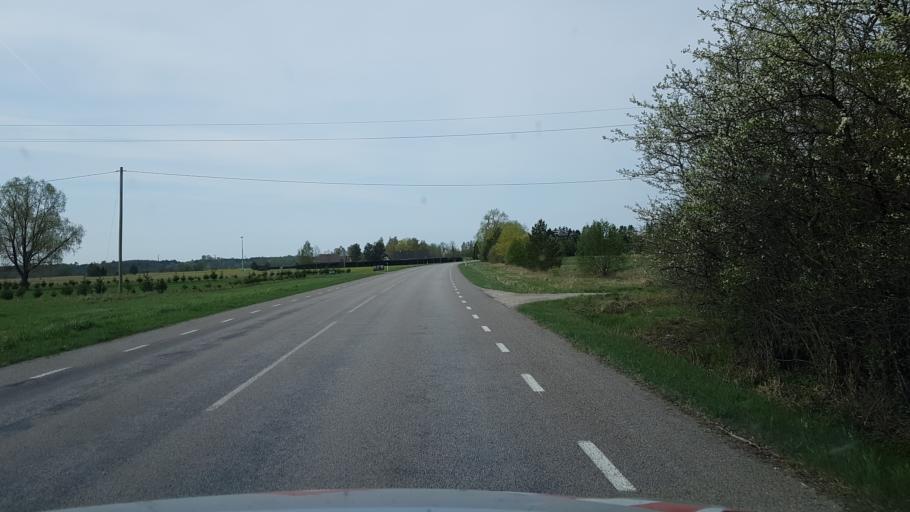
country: EE
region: Paernumaa
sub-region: Audru vald
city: Audru
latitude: 58.3692
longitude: 24.2678
